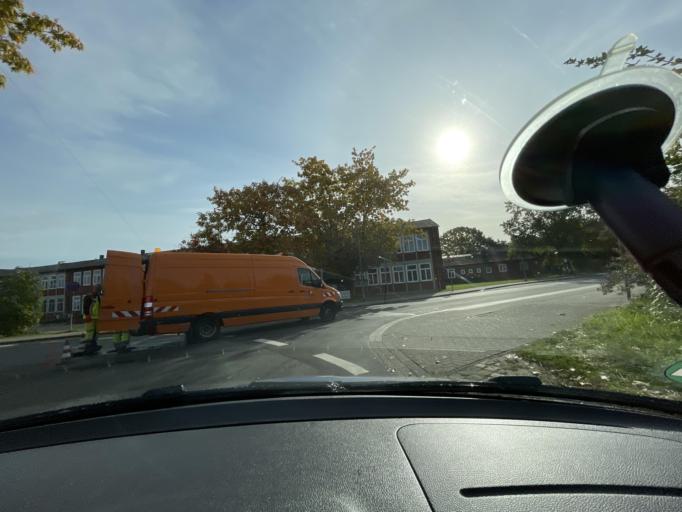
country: DE
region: Lower Saxony
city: Celle
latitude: 52.6388
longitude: 10.1111
